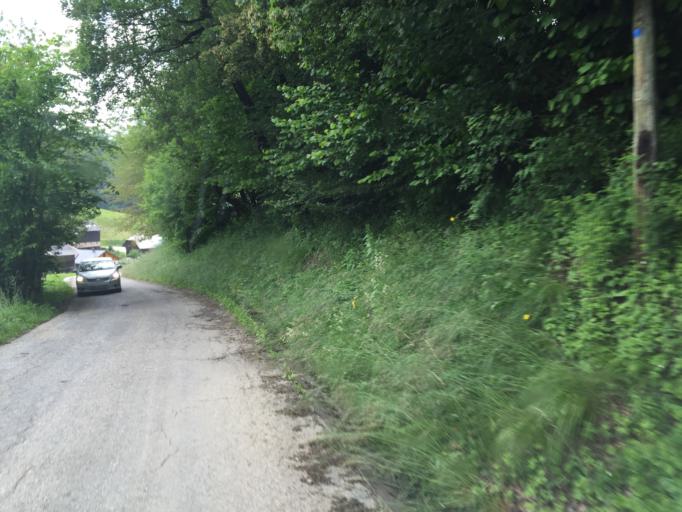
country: FR
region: Rhone-Alpes
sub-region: Departement de la Savoie
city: Cruet
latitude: 45.6111
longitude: 6.1077
